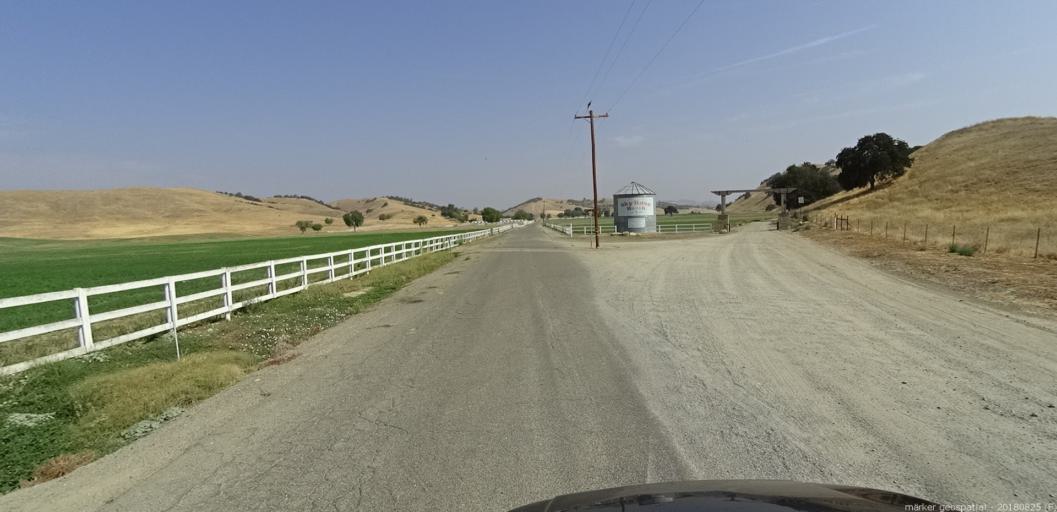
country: US
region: California
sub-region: San Luis Obispo County
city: San Miguel
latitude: 35.8240
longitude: -120.6565
